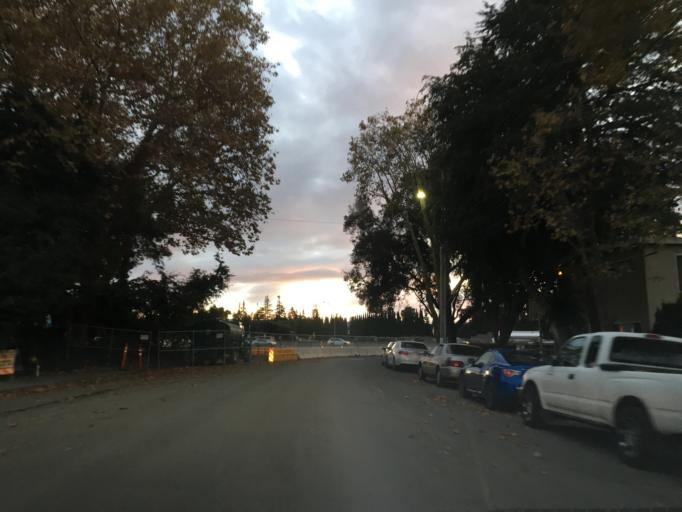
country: US
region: California
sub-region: San Mateo County
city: East Palo Alto
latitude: 37.4706
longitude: -122.1559
